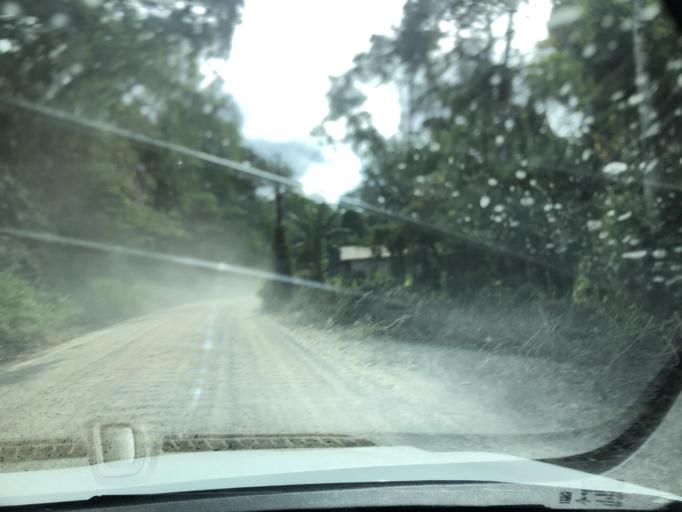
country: BR
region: Santa Catarina
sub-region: Sao Francisco Do Sul
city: Sao Francisco do Sul
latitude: -26.2261
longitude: -48.5966
